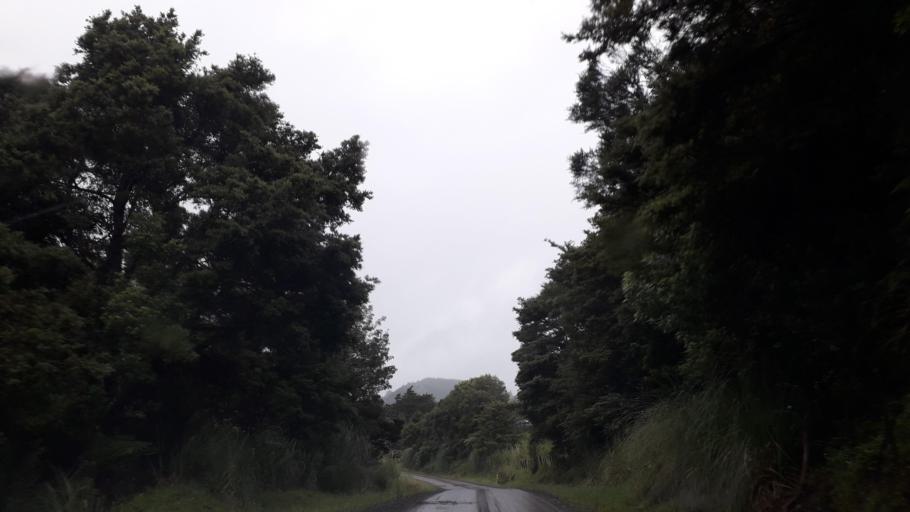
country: NZ
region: Northland
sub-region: Far North District
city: Kaitaia
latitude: -35.3834
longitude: 173.4096
